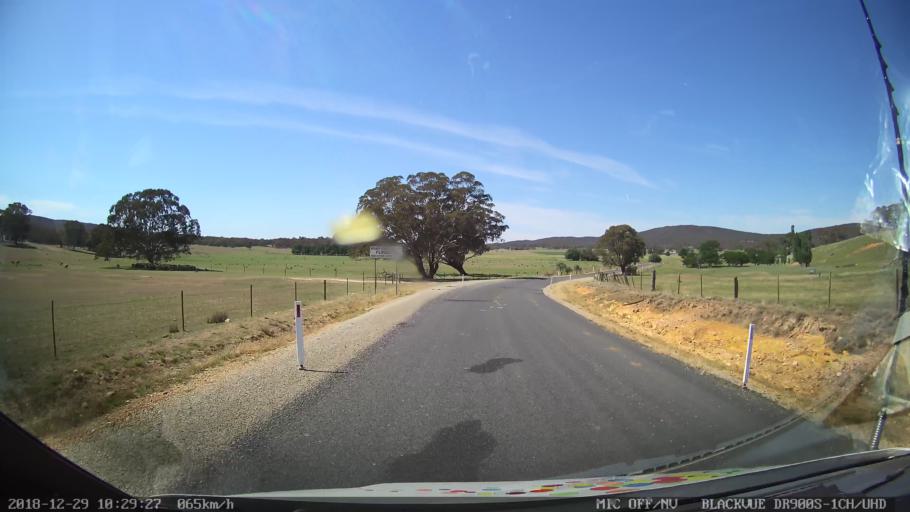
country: AU
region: New South Wales
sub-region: Yass Valley
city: Gundaroo
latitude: -34.9521
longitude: 149.4575
